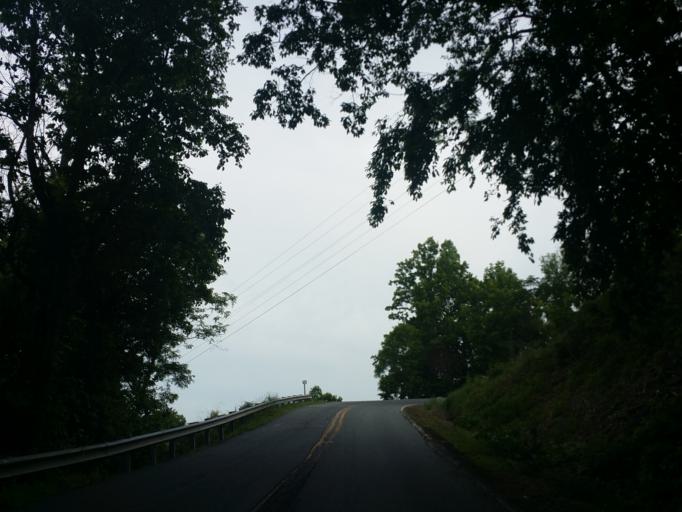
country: US
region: North Carolina
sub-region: Madison County
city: Marshall
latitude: 35.7053
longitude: -82.8248
